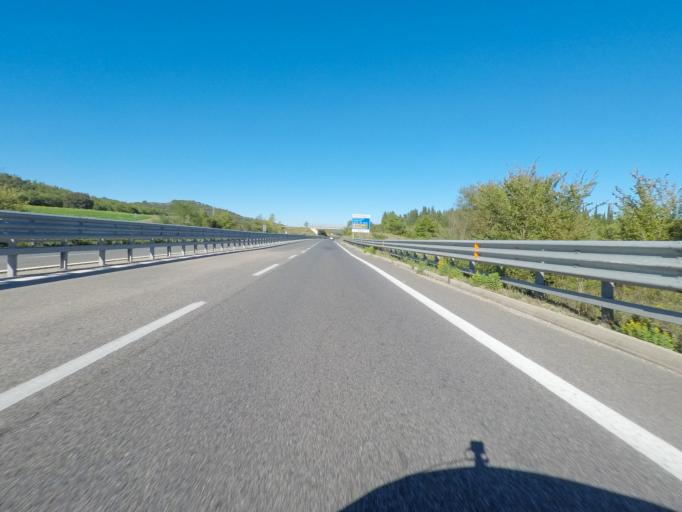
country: IT
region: Tuscany
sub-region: Provincia di Grosseto
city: Campagnatico
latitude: 42.9143
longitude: 11.2544
